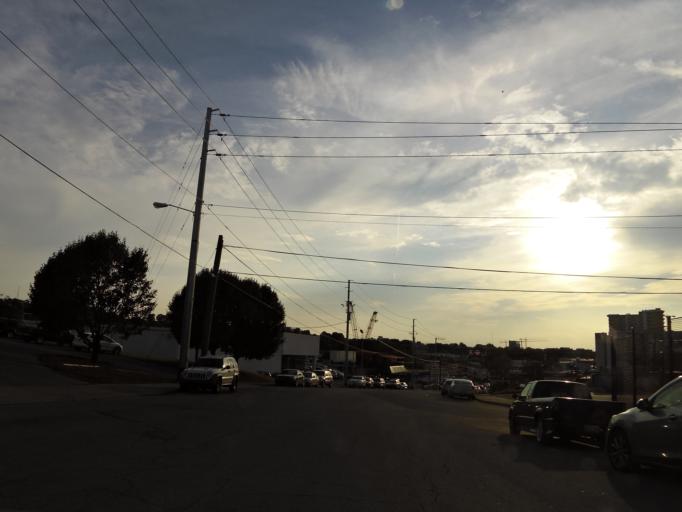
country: US
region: Tennessee
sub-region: Davidson County
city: Nashville
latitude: 36.1499
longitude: -86.7773
